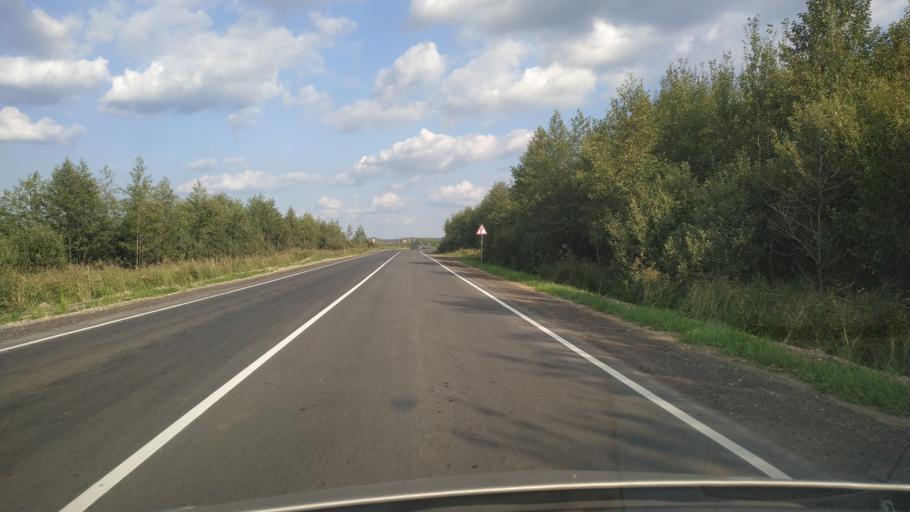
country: RU
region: Moskovskaya
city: Vereya
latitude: 55.7224
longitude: 39.0559
